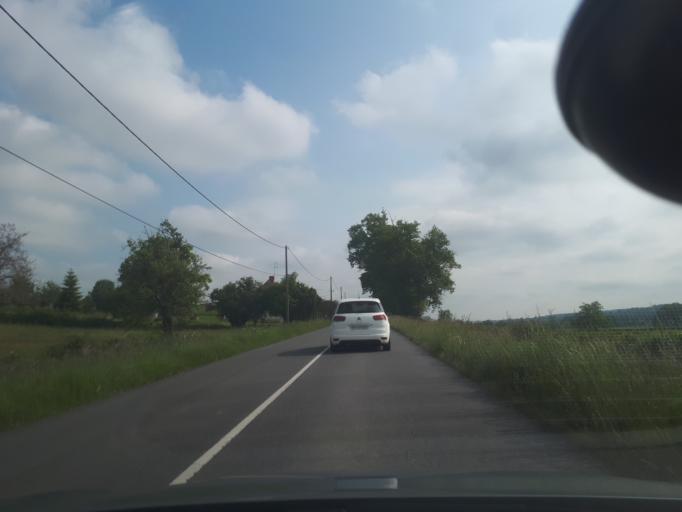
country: FR
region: Auvergne
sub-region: Departement de l'Allier
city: Dompierre-sur-Besbre
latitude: 46.4028
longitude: 3.5999
